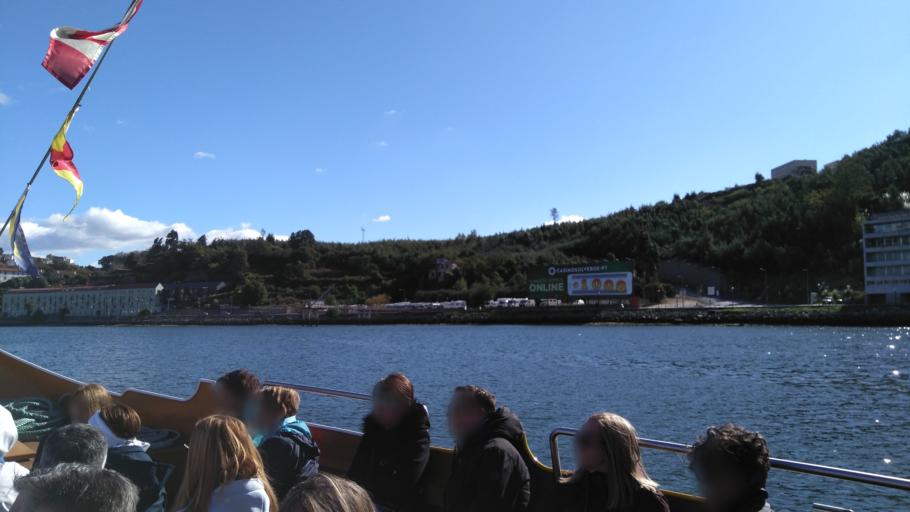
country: PT
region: Porto
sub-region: Vila Nova de Gaia
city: Vila Nova de Gaia
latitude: 41.1454
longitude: -8.6342
